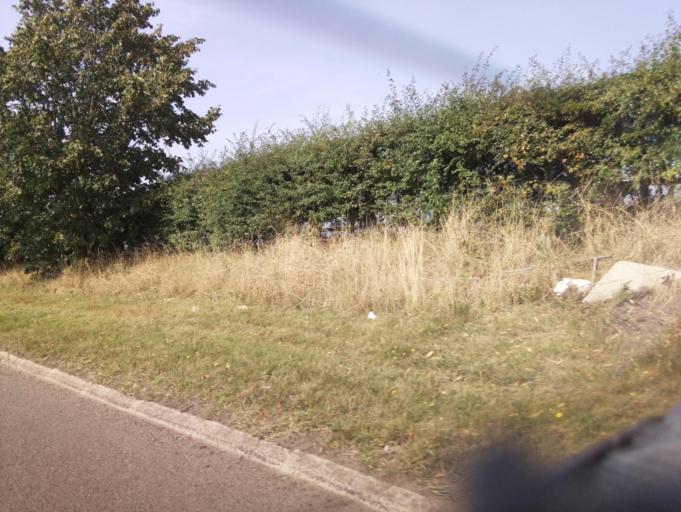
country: GB
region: England
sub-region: Staffordshire
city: Chasetown
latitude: 52.6553
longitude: -1.8834
